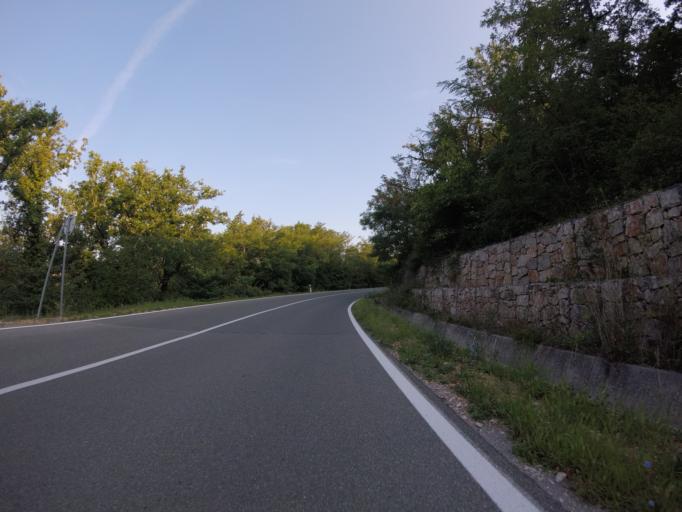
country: HR
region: Primorsko-Goranska
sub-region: Grad Crikvenica
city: Crikvenica
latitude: 45.1883
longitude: 14.7132
